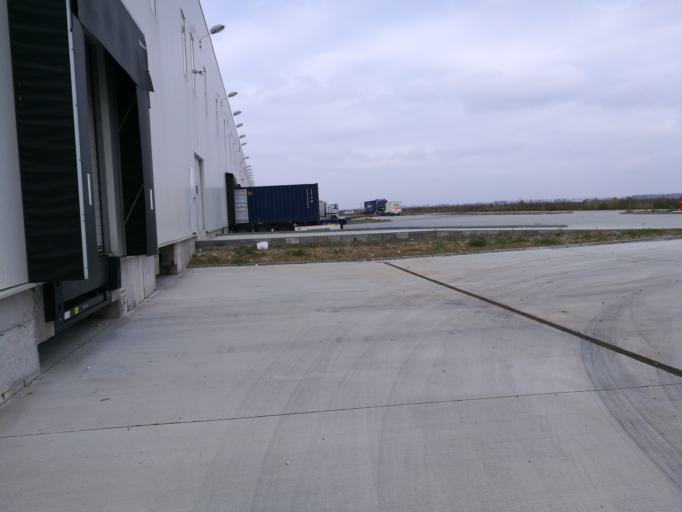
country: RO
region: Giurgiu
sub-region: Comuna Bolintin Deal
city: Bolintin Deal
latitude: 44.4610
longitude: 25.8538
